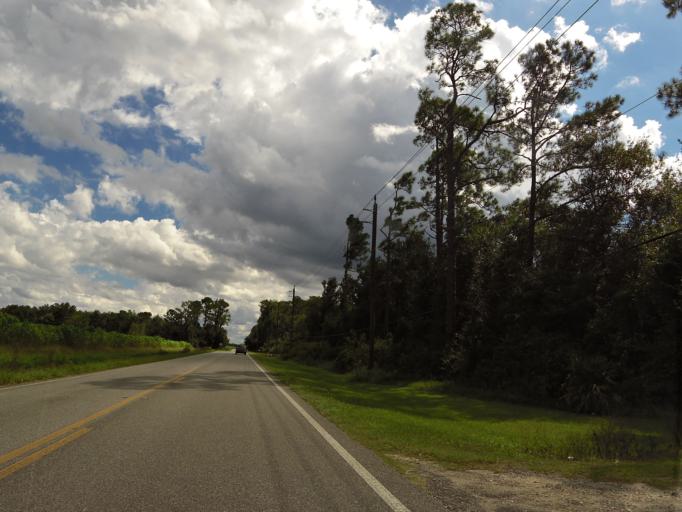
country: US
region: Florida
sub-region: Saint Johns County
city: Saint Augustine South
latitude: 29.8151
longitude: -81.4847
